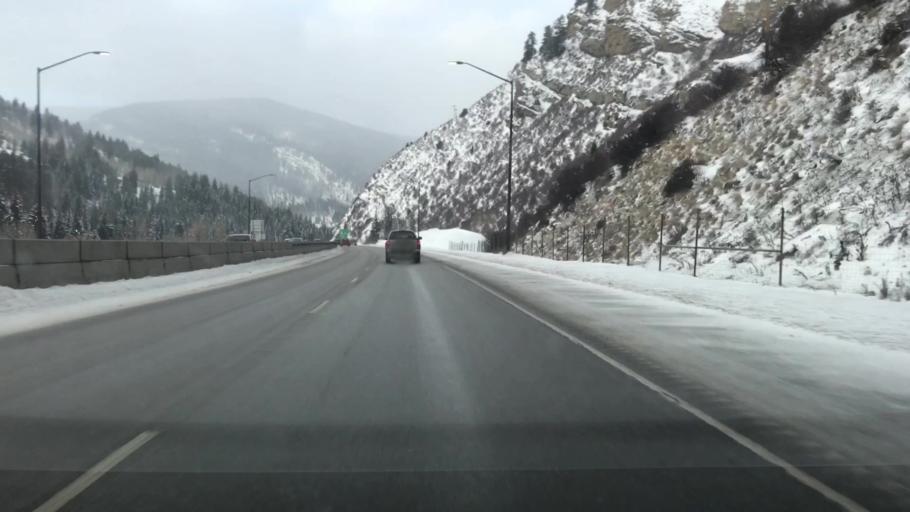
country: US
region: Colorado
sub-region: Eagle County
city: Minturn
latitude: 39.6192
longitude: -106.4336
